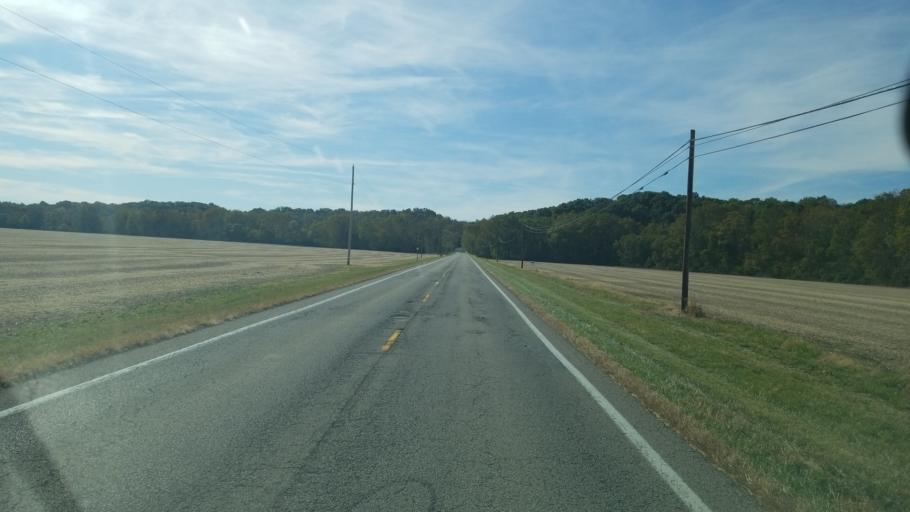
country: US
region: Ohio
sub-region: Clinton County
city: Blanchester
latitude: 39.4014
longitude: -83.9943
